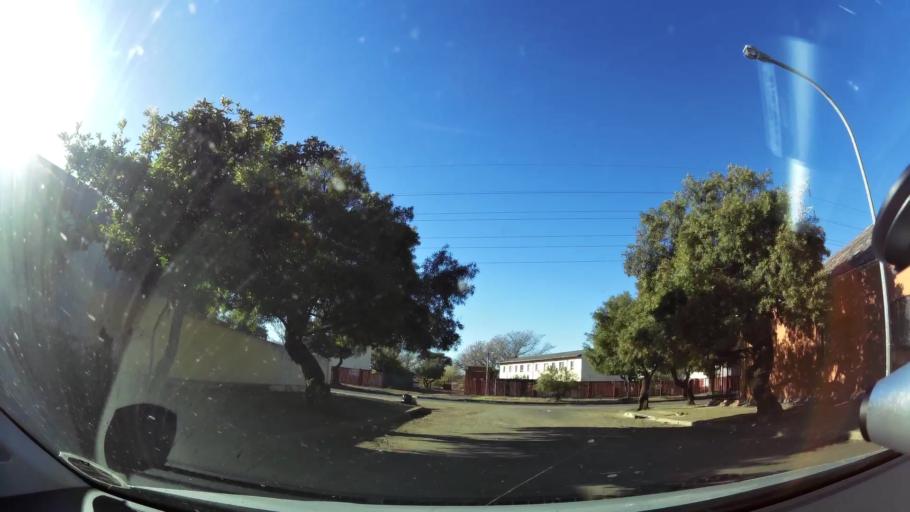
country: ZA
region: Northern Cape
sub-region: Frances Baard District Municipality
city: Kimberley
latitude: -28.7552
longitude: 24.7880
